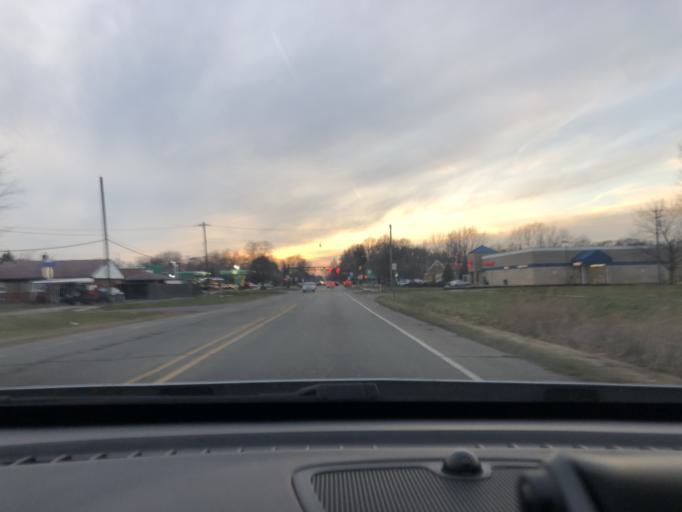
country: US
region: Michigan
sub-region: Wayne County
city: Taylor
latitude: 42.2411
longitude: -83.2672
